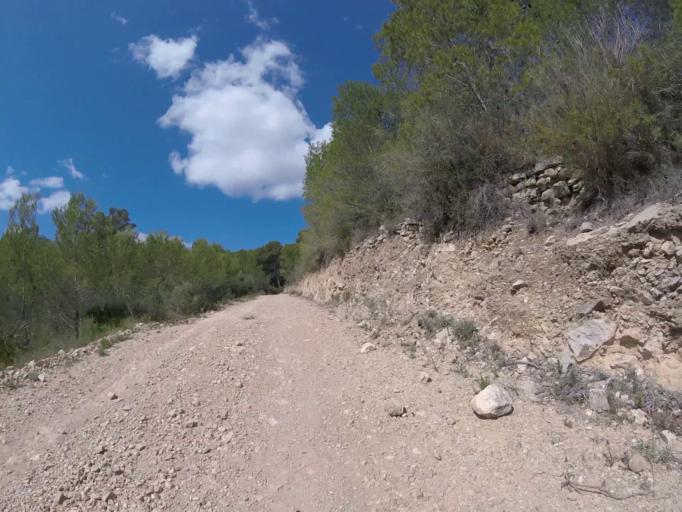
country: ES
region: Valencia
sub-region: Provincia de Castello
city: Santa Magdalena de Pulpis
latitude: 40.3114
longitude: 0.3233
